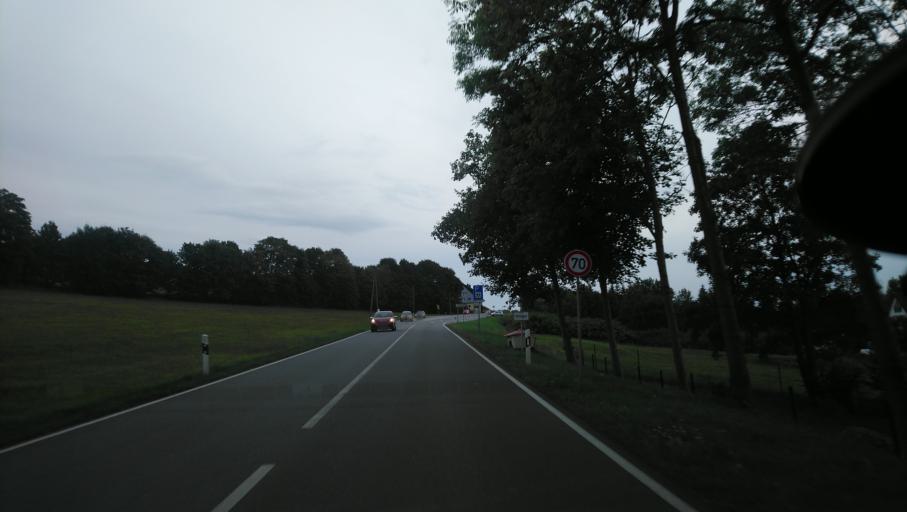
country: DE
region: Saxony
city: Ehrenfriedersdorf
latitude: 50.6377
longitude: 12.9657
